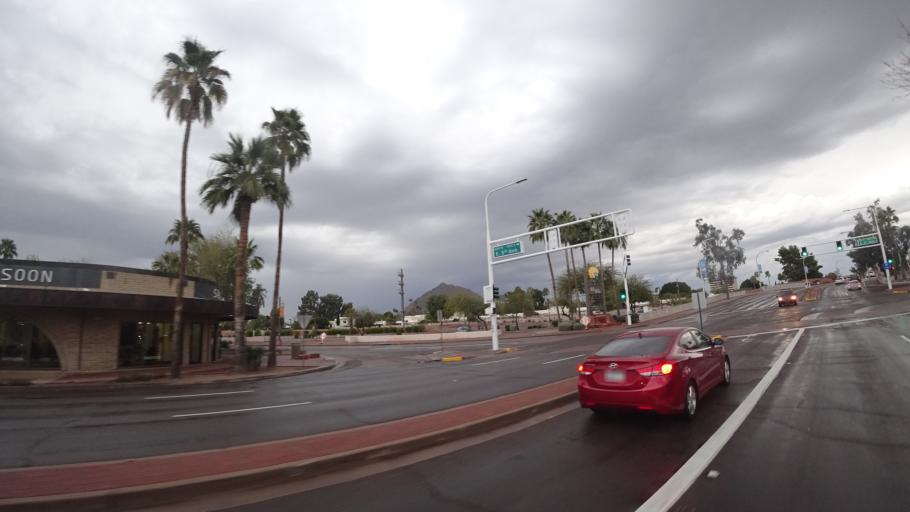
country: US
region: Arizona
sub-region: Maricopa County
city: Scottsdale
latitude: 33.4967
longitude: -111.9303
